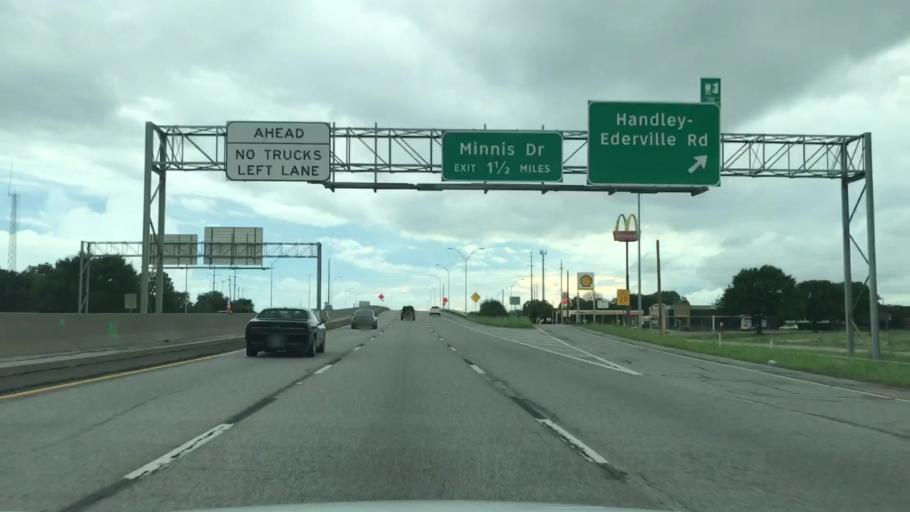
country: US
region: Texas
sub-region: Tarrant County
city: Richland Hills
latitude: 32.8027
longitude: -97.2181
